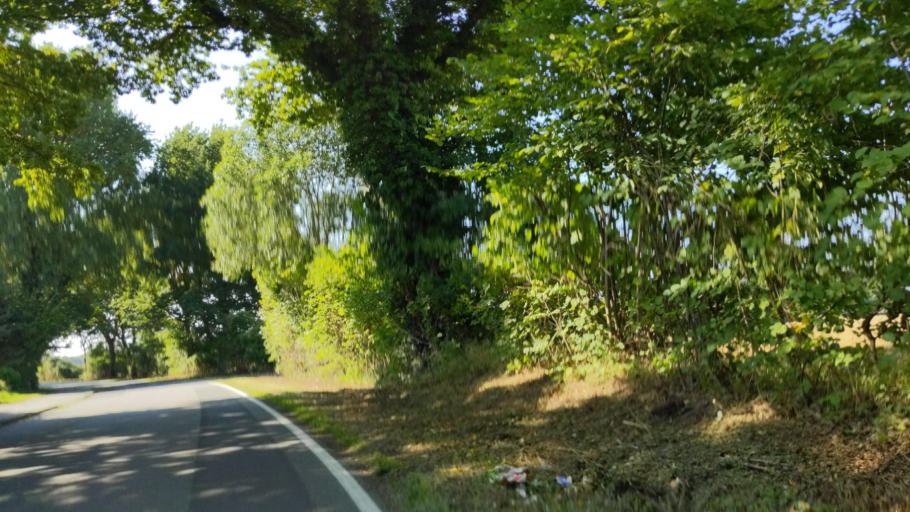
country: DE
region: Schleswig-Holstein
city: Gross Schenkenberg
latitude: 53.7990
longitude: 10.5842
